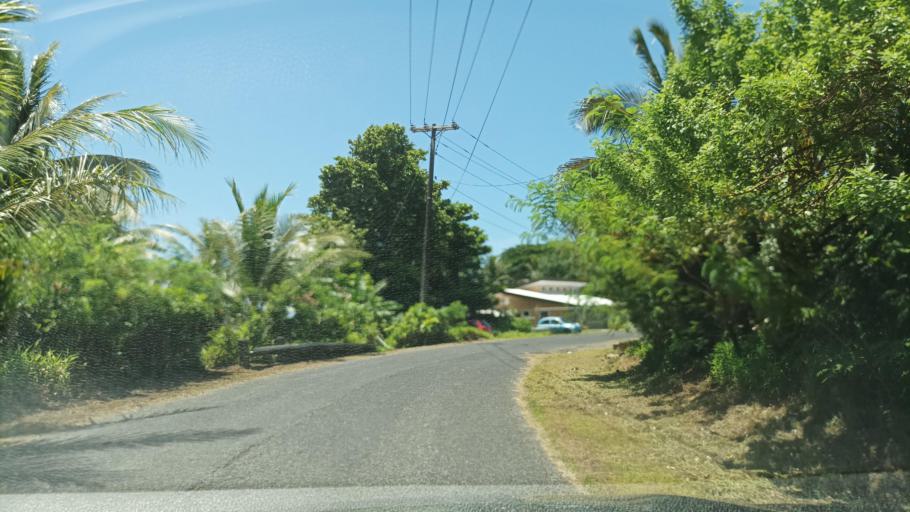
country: FM
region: Pohnpei
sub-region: Kolonia Municipality
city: Kolonia
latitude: 6.9633
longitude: 158.2499
